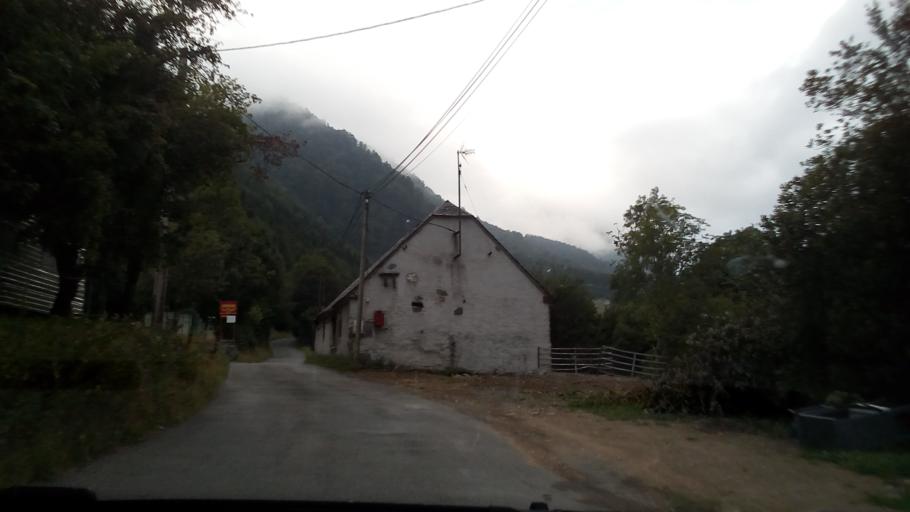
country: FR
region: Midi-Pyrenees
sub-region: Departement des Hautes-Pyrenees
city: Cauterets
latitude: 42.9171
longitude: -0.1890
